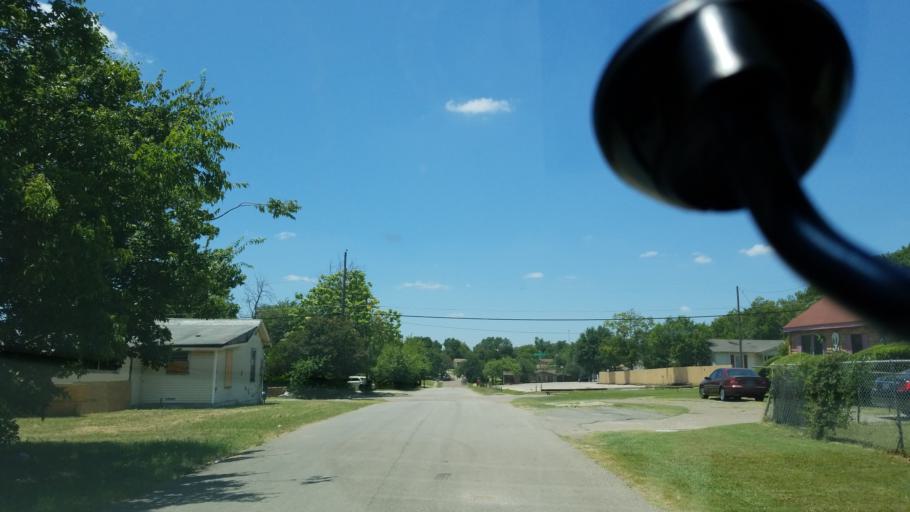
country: US
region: Texas
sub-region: Dallas County
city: Cockrell Hill
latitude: 32.6938
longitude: -96.8126
